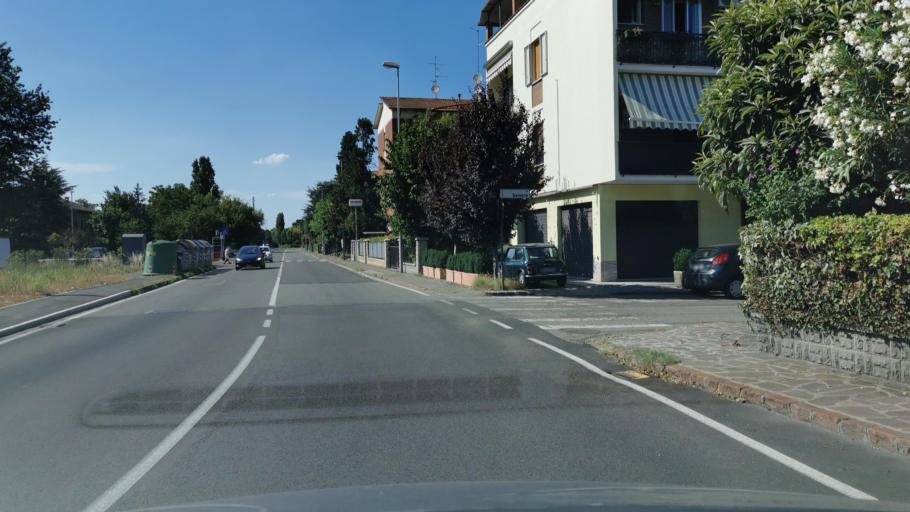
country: IT
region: Emilia-Romagna
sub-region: Provincia di Modena
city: Modena
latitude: 44.6190
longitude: 10.9310
